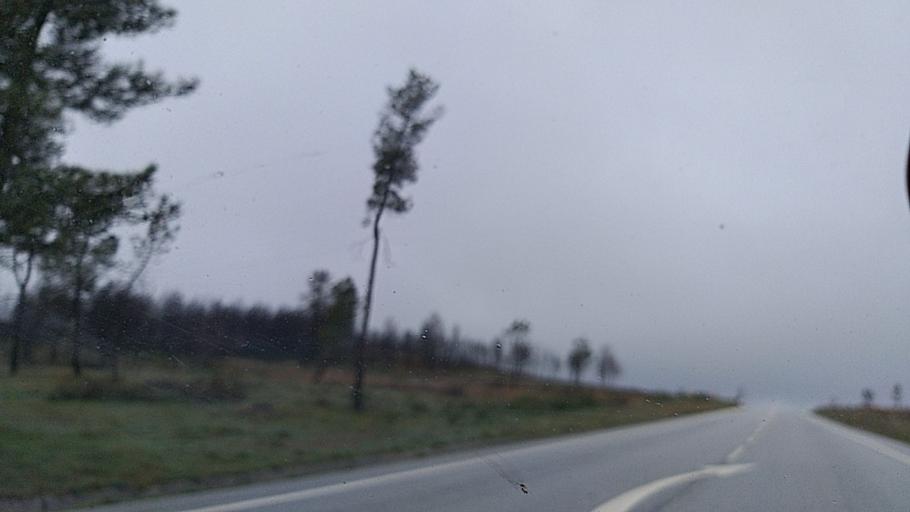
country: PT
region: Guarda
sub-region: Fornos de Algodres
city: Fornos de Algodres
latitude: 40.6997
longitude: -7.4767
